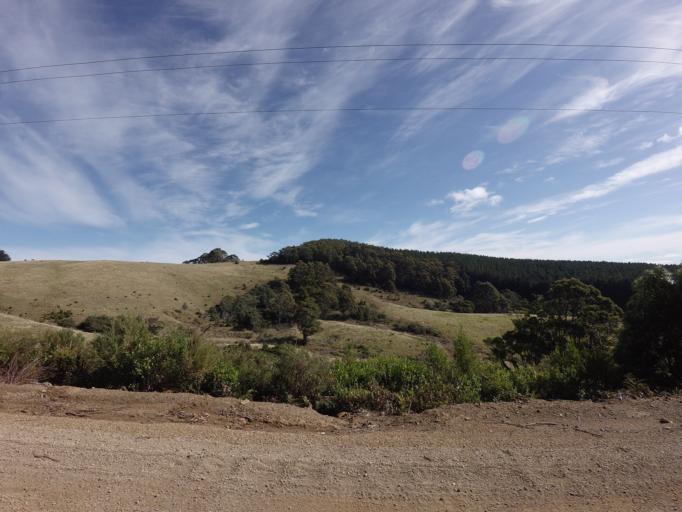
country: AU
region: Tasmania
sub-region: Clarence
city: Sandford
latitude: -43.1843
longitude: 147.7713
